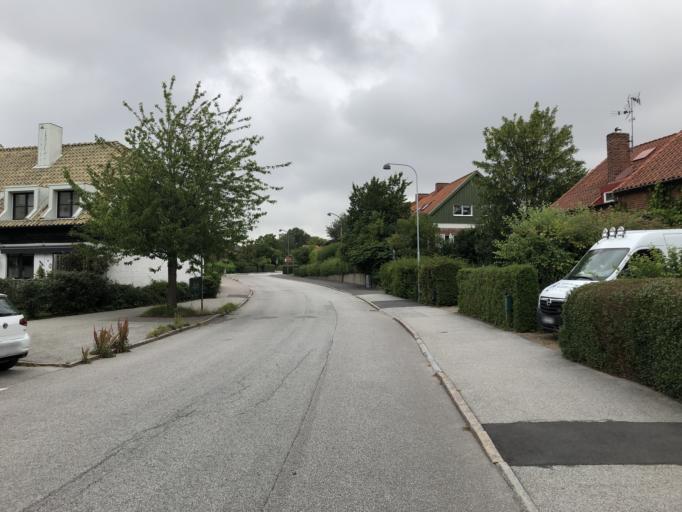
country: SE
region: Skane
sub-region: Lunds Kommun
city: Lund
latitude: 55.7017
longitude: 13.2075
